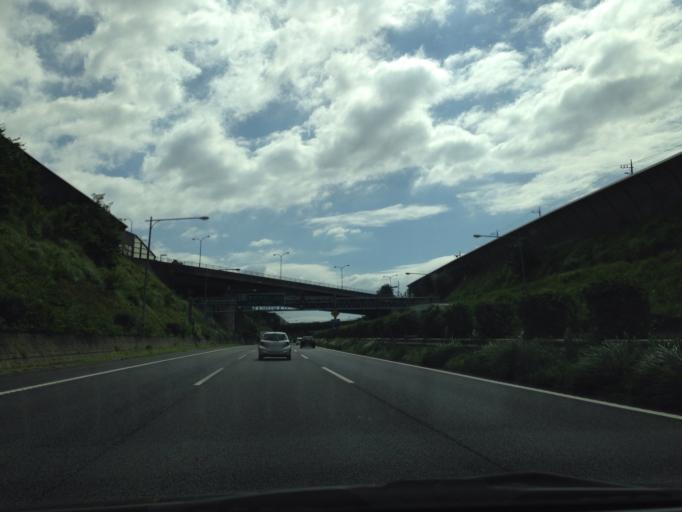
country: JP
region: Kanagawa
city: Hadano
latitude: 35.3644
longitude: 139.2573
